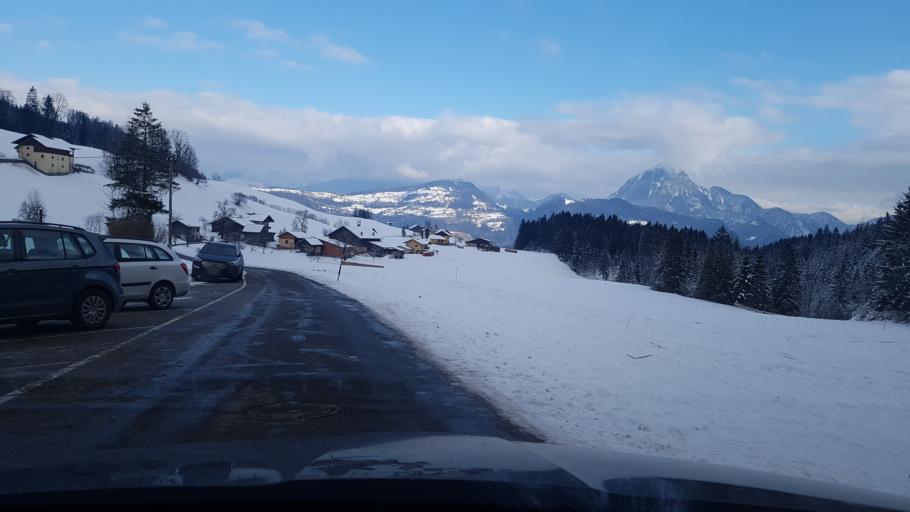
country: AT
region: Salzburg
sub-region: Politischer Bezirk Hallein
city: Kuchl
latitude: 47.6064
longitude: 13.1177
